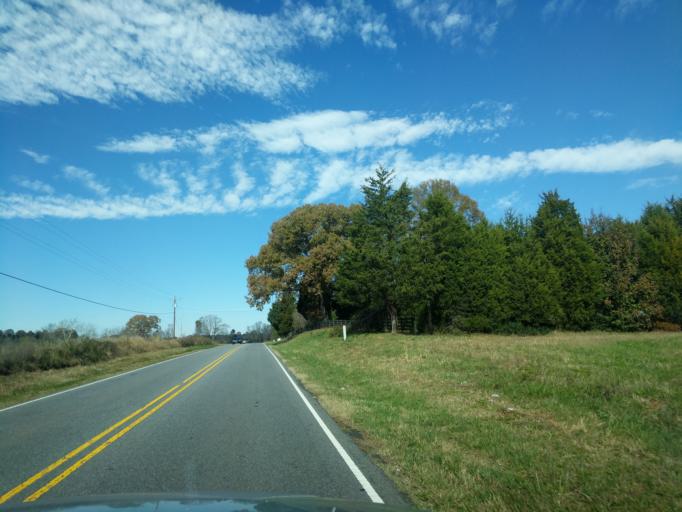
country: US
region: North Carolina
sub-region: Catawba County
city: Maiden
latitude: 35.6140
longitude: -81.2571
